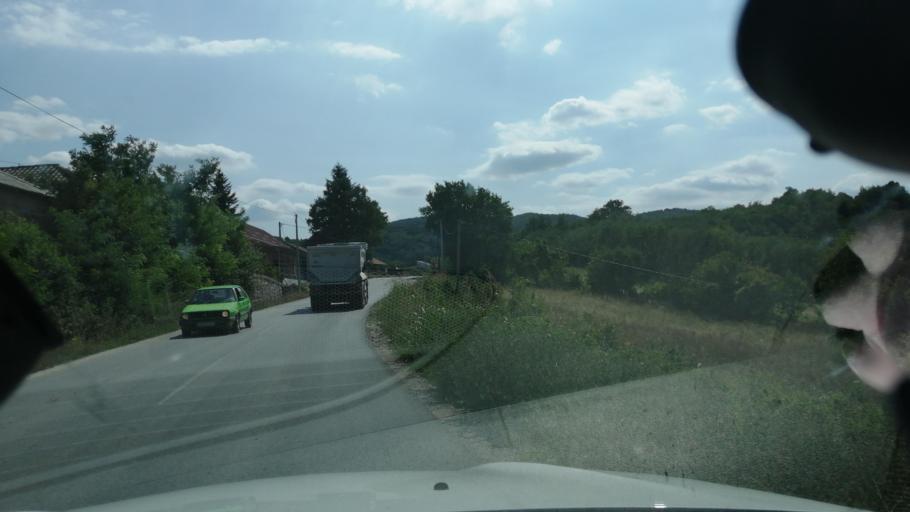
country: RS
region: Central Serbia
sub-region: Moravicki Okrug
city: Cacak
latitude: 43.8569
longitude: 20.3083
